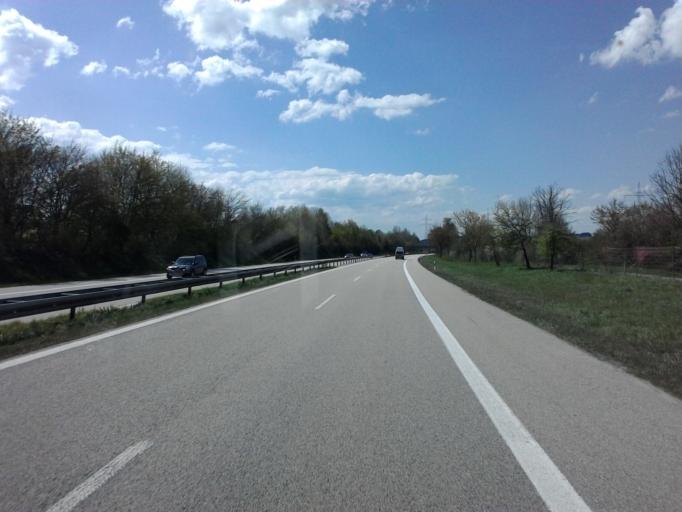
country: DE
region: Bavaria
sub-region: Swabia
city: Nesselwang
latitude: 47.6422
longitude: 10.4997
